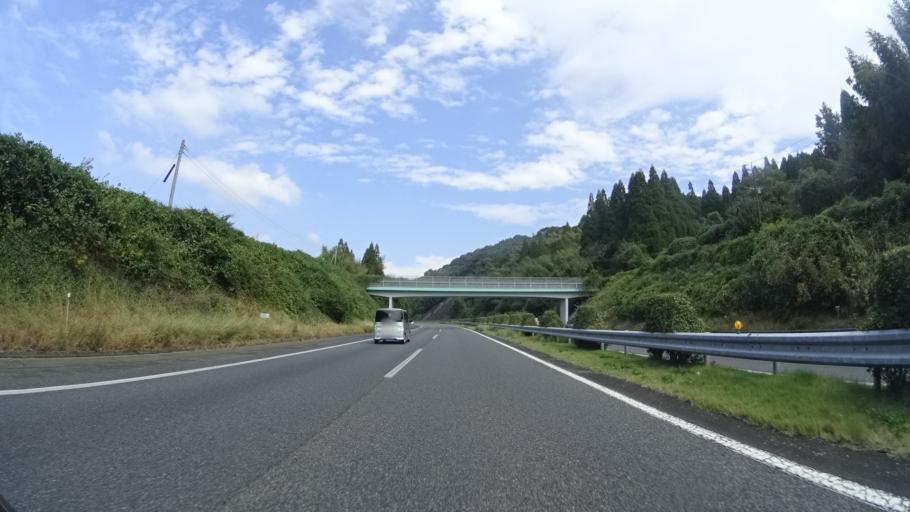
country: JP
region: Kumamoto
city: Matsubase
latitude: 32.6071
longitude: 130.7230
